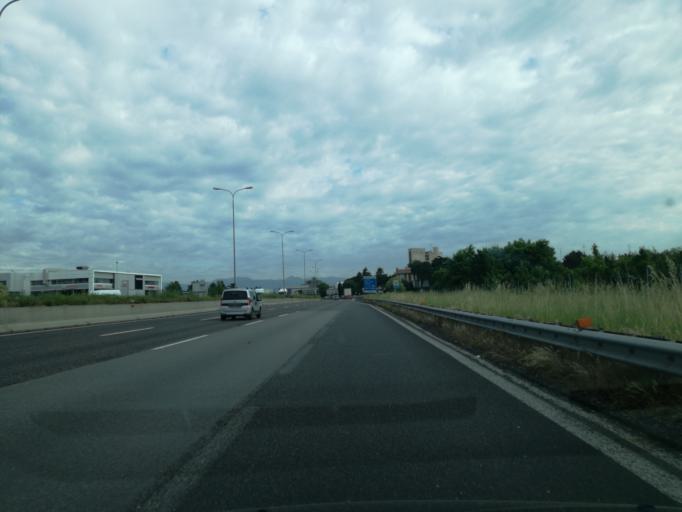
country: IT
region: Lombardy
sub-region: Provincia di Monza e Brianza
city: Santa Margherita
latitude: 45.6536
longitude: 9.2261
